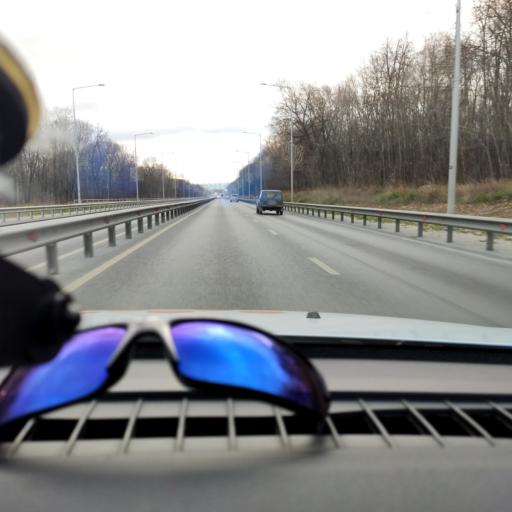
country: RU
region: Samara
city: Volzhskiy
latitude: 53.3625
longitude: 50.2029
